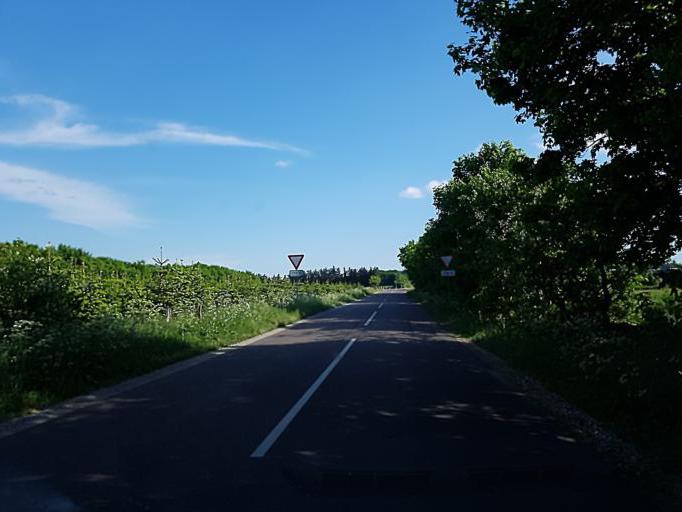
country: DK
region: South Denmark
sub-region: Varde Kommune
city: Varde
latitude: 55.5808
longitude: 8.4145
